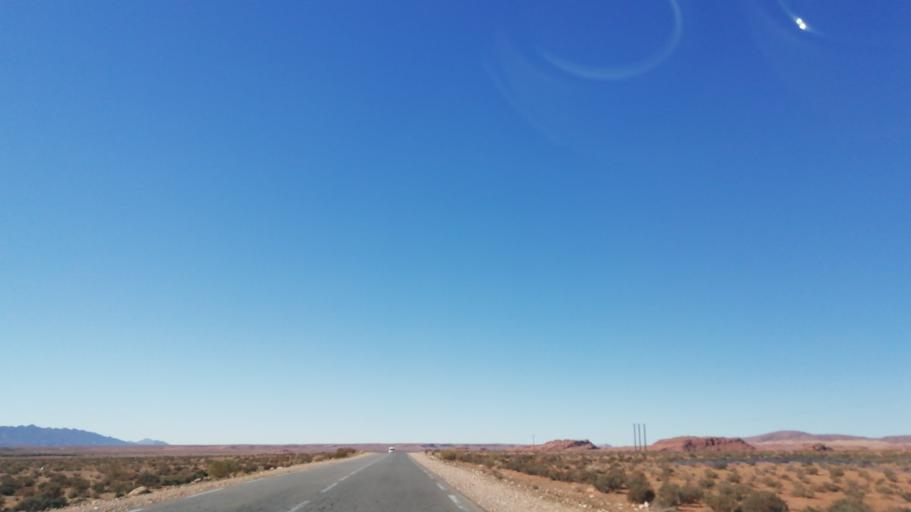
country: DZ
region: El Bayadh
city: El Abiodh Sidi Cheikh
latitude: 33.1801
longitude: 0.5442
